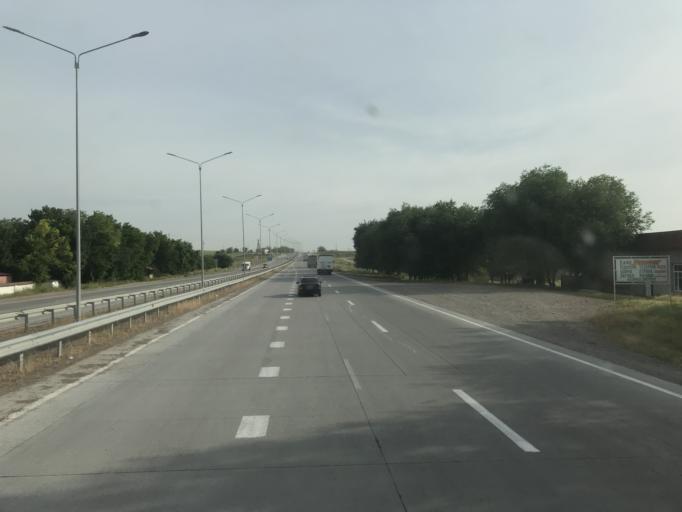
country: KZ
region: Ongtustik Qazaqstan
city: Qazyqurt
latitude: 41.7990
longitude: 69.3940
